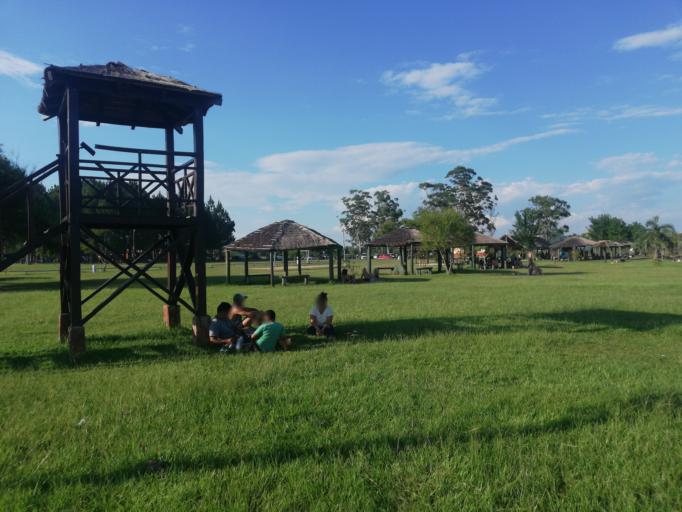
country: AR
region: Corrientes
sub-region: Departamento de San Miguel
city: San Miguel
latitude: -28.0068
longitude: -57.5932
